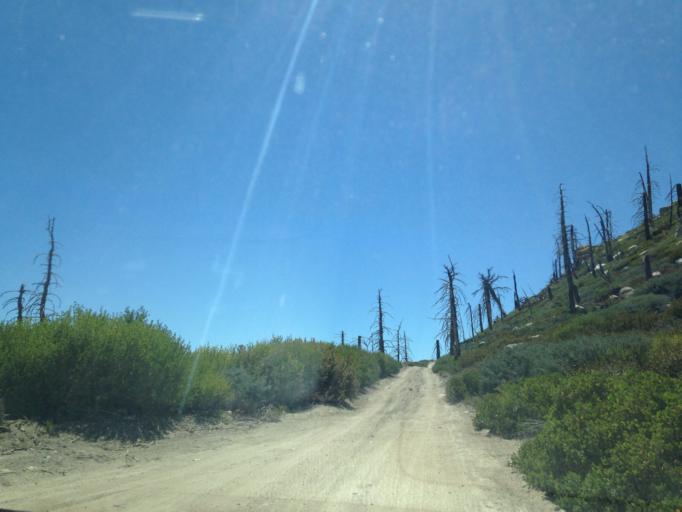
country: US
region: California
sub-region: San Bernardino County
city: Big Bear Lake
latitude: 34.2565
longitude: -117.0000
